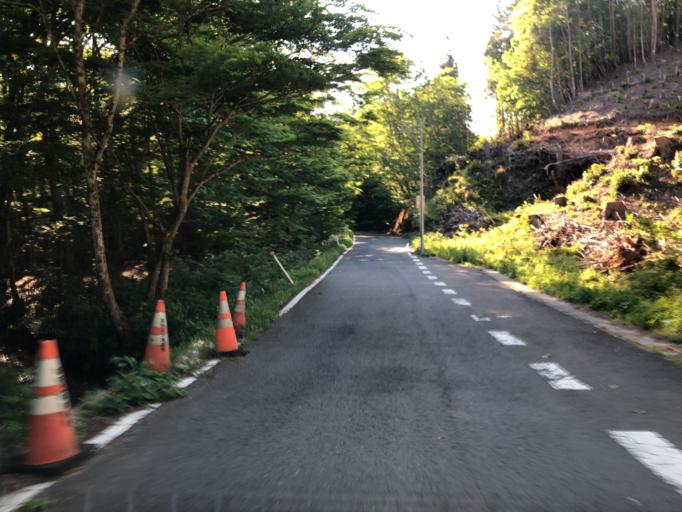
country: JP
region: Ibaraki
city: Kitaibaraki
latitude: 36.8977
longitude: 140.5965
